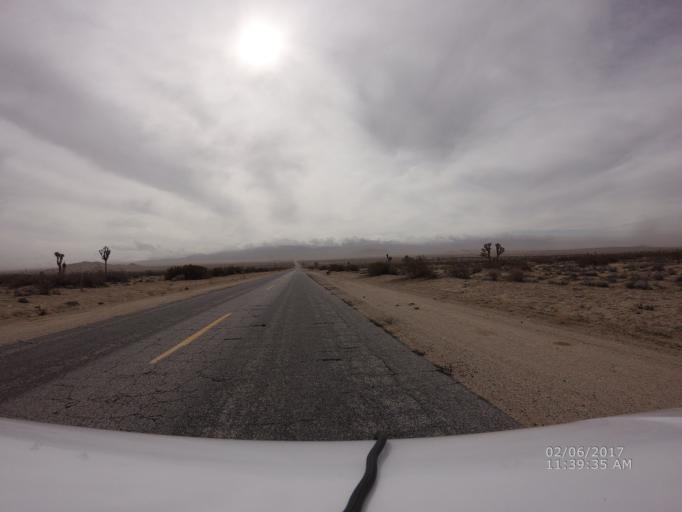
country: US
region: California
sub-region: Los Angeles County
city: Lake Los Angeles
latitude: 34.6227
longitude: -117.7027
